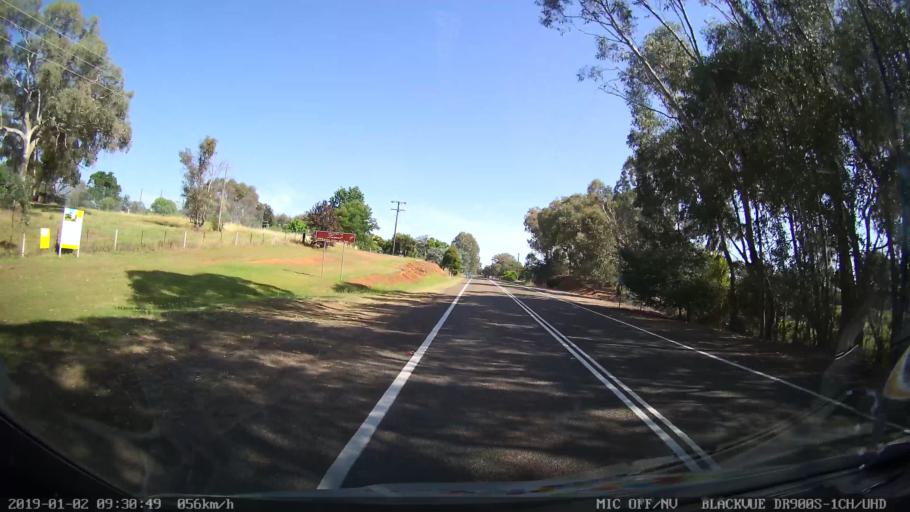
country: AU
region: New South Wales
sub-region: Tumut Shire
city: Tumut
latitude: -35.3235
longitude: 148.2378
